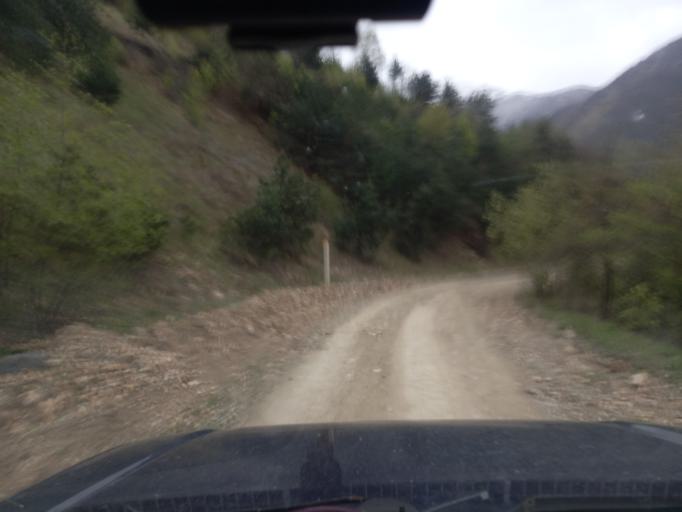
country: RU
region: North Ossetia
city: Mizur
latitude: 42.8532
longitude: 44.1647
